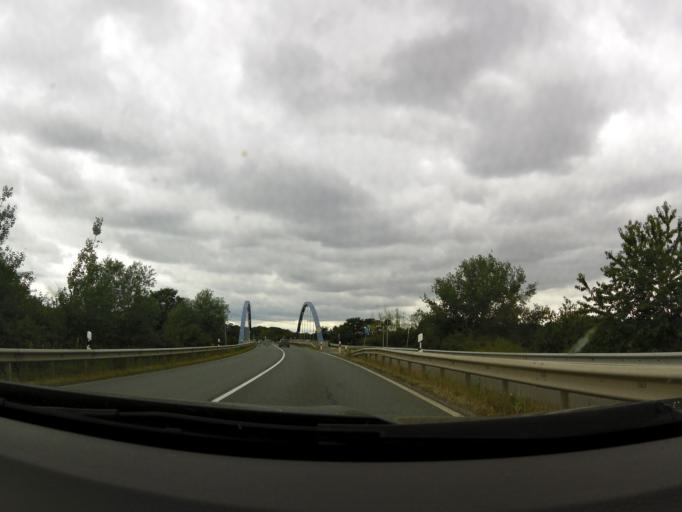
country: DE
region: North Rhine-Westphalia
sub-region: Regierungsbezirk Dusseldorf
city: Voerde
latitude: 51.6348
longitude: 6.6848
